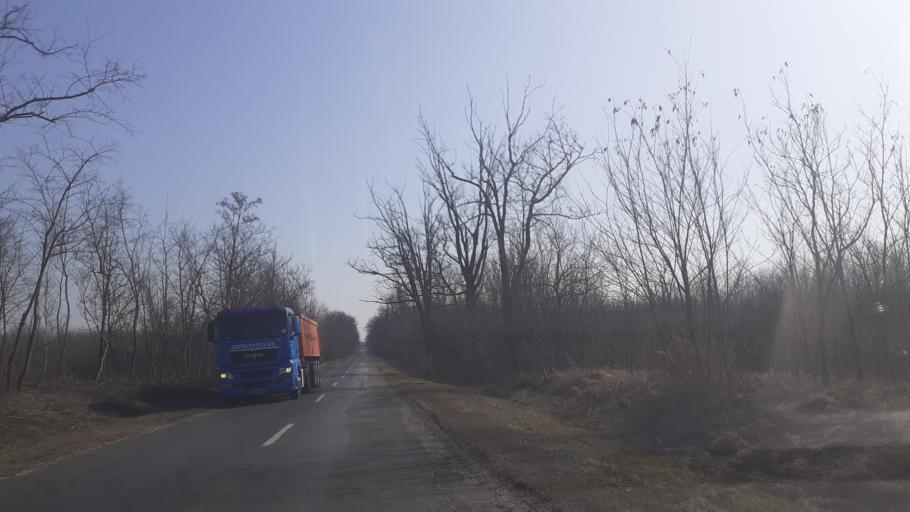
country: HU
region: Pest
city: Orkeny
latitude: 47.0693
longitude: 19.3879
